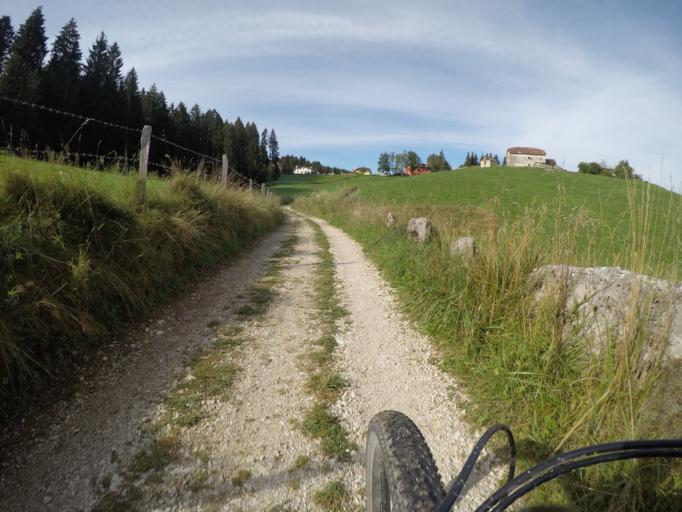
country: IT
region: Veneto
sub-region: Provincia di Vicenza
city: Asiago
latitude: 45.8561
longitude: 11.5087
